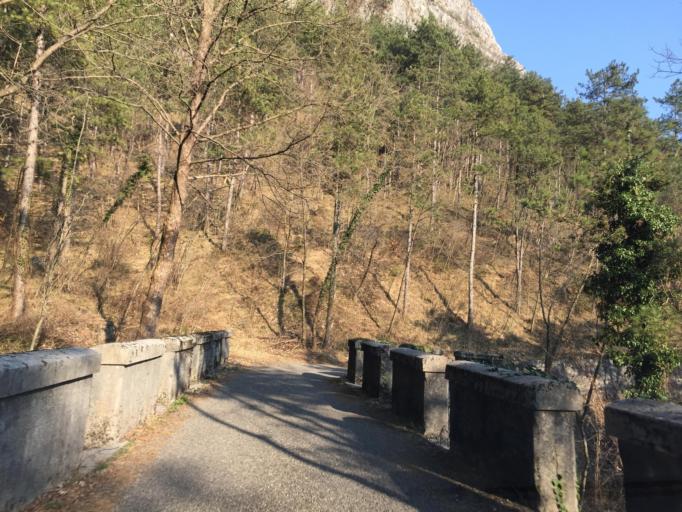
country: IT
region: Friuli Venezia Giulia
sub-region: Provincia di Udine
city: Amaro
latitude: 46.3811
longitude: 13.0887
